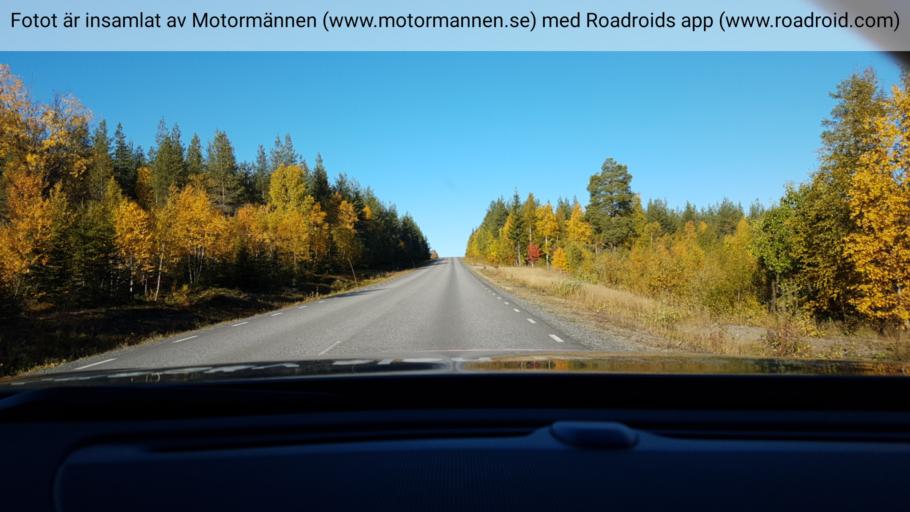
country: SE
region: Vaesterbotten
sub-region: Skelleftea Kommun
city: Storvik
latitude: 65.3245
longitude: 20.7657
